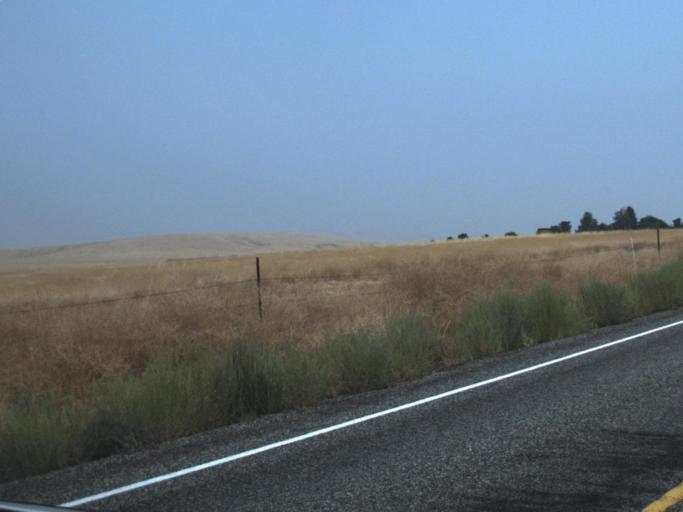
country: US
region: Washington
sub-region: Yakima County
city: Sunnyside
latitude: 46.3949
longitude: -119.9523
